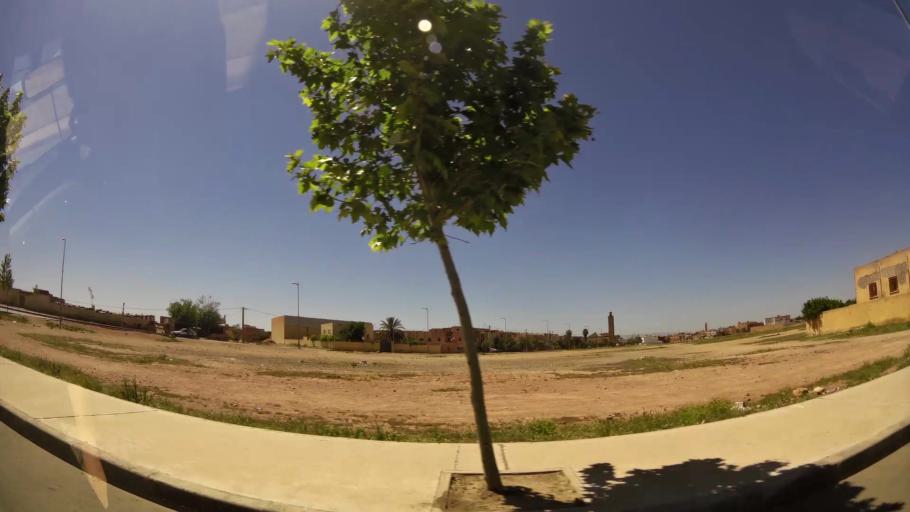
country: MA
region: Oriental
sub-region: Oujda-Angad
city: Oujda
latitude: 34.6627
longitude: -1.8660
